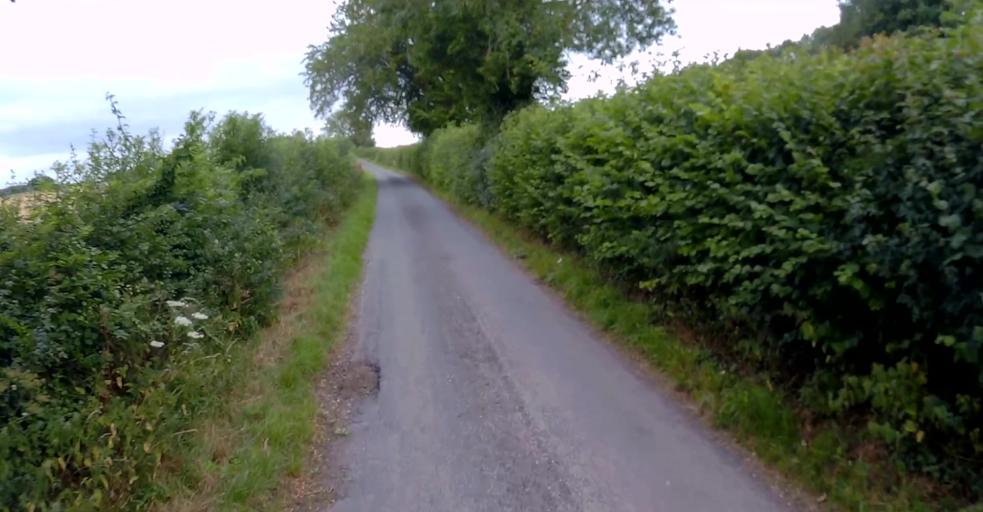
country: GB
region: England
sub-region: Hampshire
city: Kings Worthy
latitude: 51.0575
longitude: -1.2079
